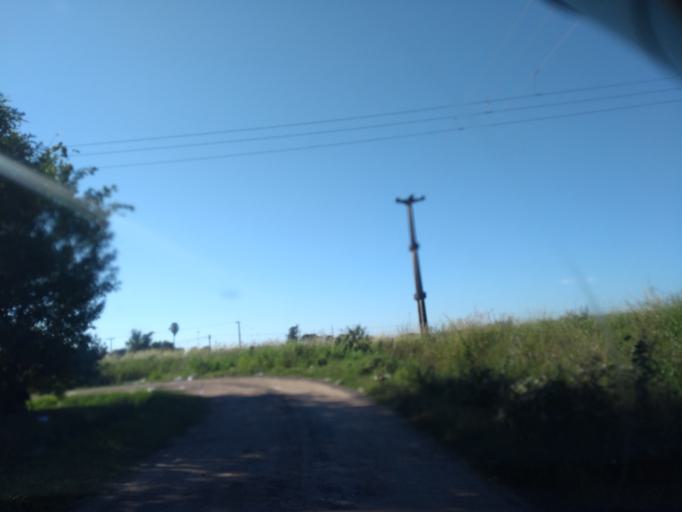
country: AR
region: Chaco
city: Fontana
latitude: -27.4197
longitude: -59.0454
